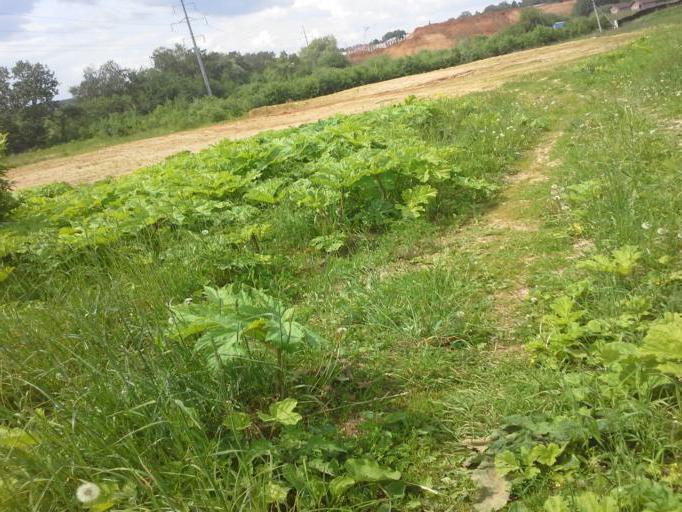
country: RU
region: Moskovskaya
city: Lesnoy Gorodok
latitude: 55.6533
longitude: 37.1855
